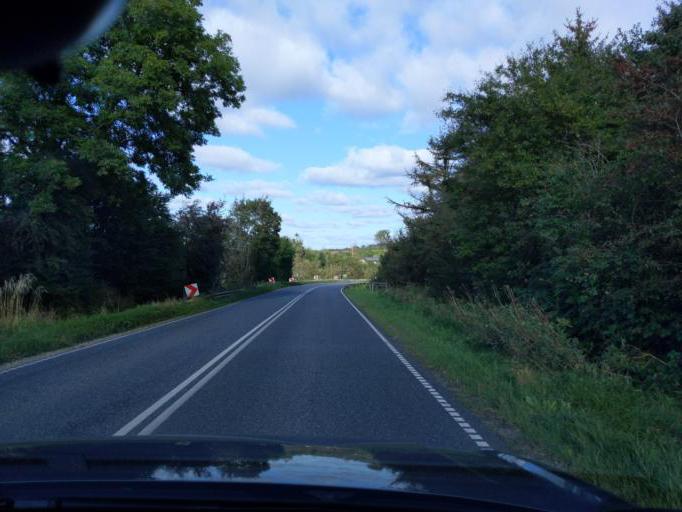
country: DK
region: Central Jutland
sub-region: Viborg Kommune
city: Bjerringbro
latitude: 56.5002
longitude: 9.5841
